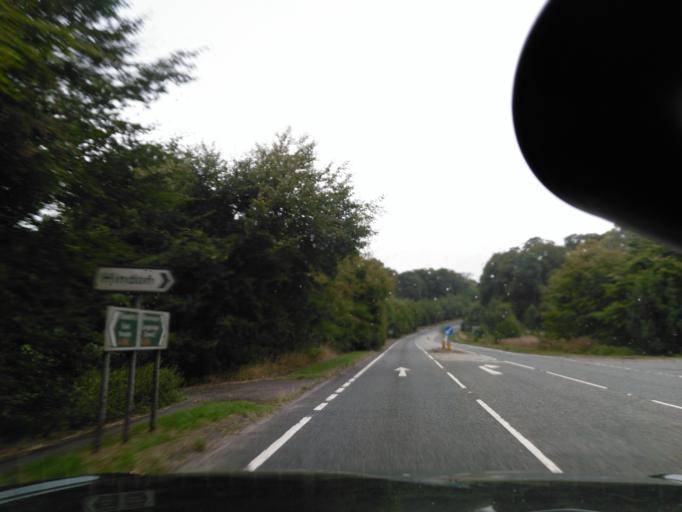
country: GB
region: England
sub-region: Wiltshire
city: Hindon
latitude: 51.0769
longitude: -2.1681
